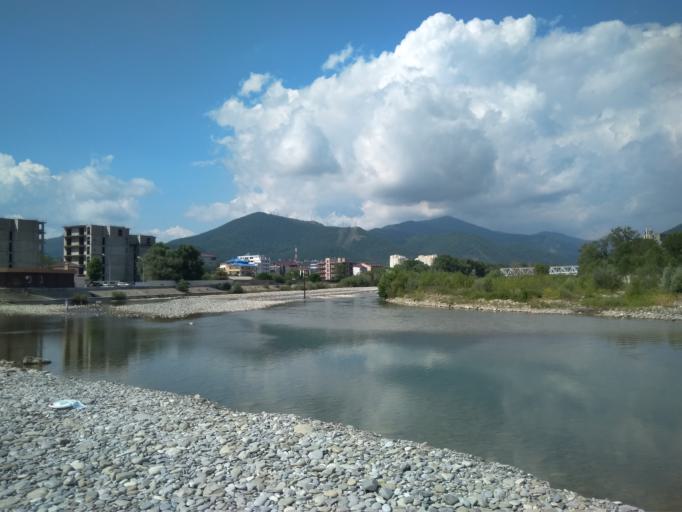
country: RU
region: Krasnodarskiy
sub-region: Sochi City
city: Lazarevskoye
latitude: 43.8982
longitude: 39.3340
